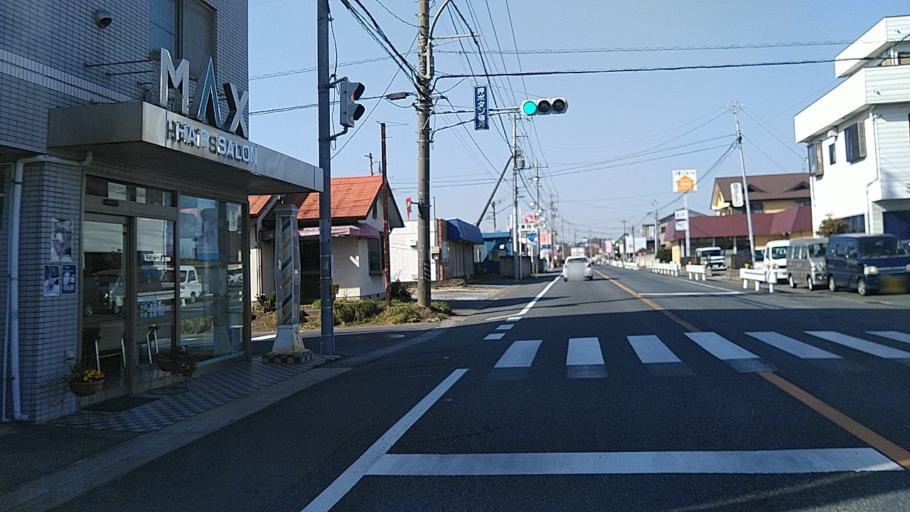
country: JP
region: Saitama
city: Fukiage-fujimi
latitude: 36.0688
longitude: 139.4078
